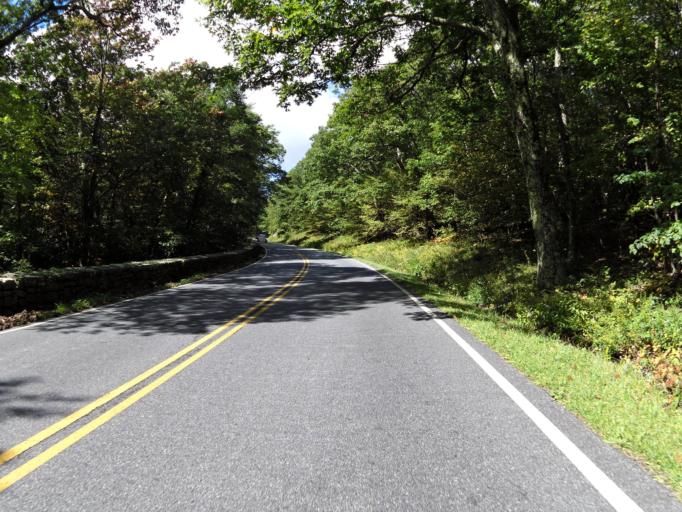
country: US
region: Virginia
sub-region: Page County
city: Luray
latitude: 38.5879
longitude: -78.3694
